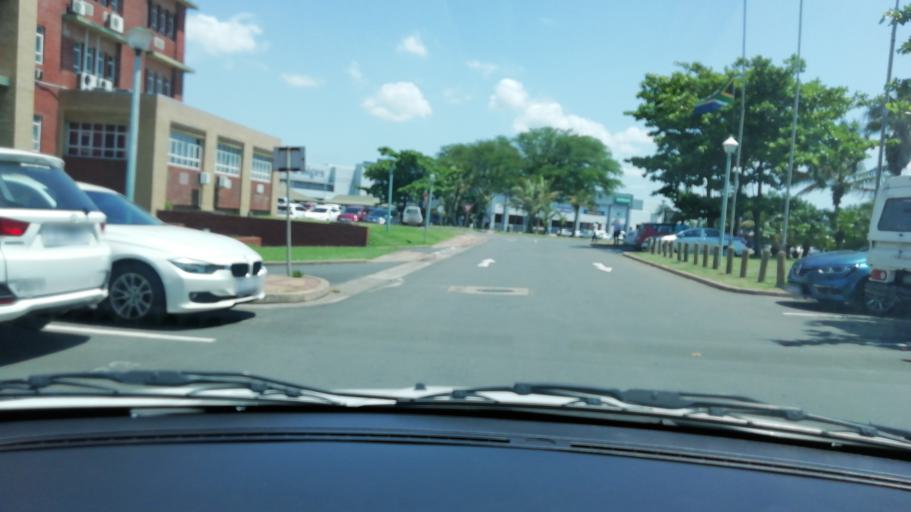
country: ZA
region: KwaZulu-Natal
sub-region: uThungulu District Municipality
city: Richards Bay
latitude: -28.7555
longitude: 32.0508
